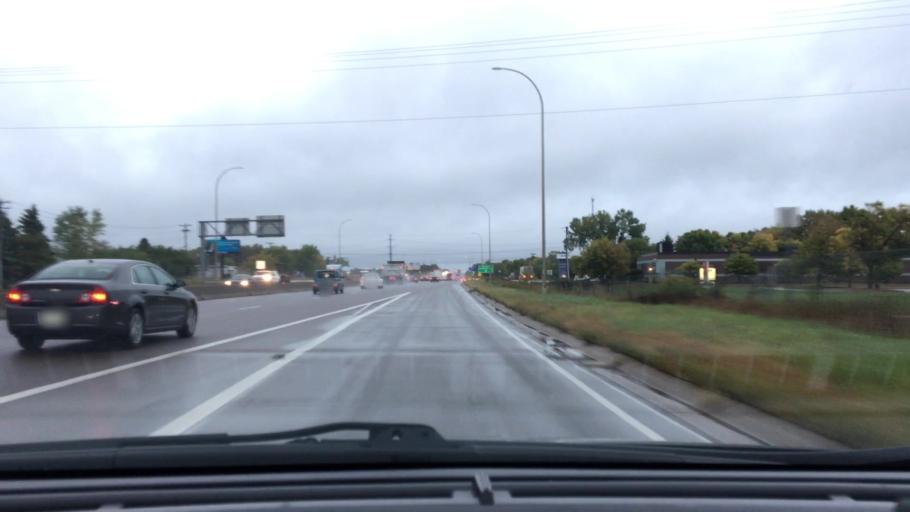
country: US
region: Minnesota
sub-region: Hennepin County
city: New Hope
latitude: 44.9856
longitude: -93.4005
